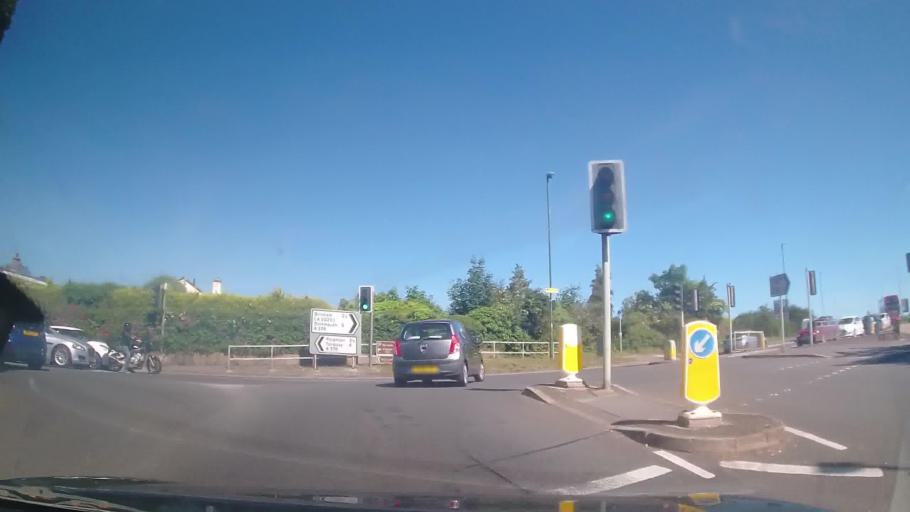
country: GB
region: England
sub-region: Borough of Torbay
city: Paignton
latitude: 50.4025
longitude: -3.5655
